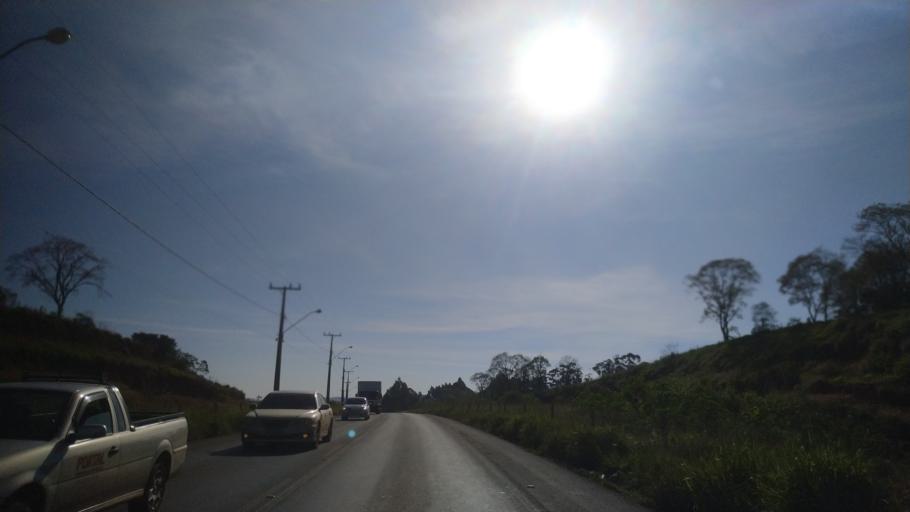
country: BR
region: Santa Catarina
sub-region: Chapeco
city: Chapeco
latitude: -27.1190
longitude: -52.6324
